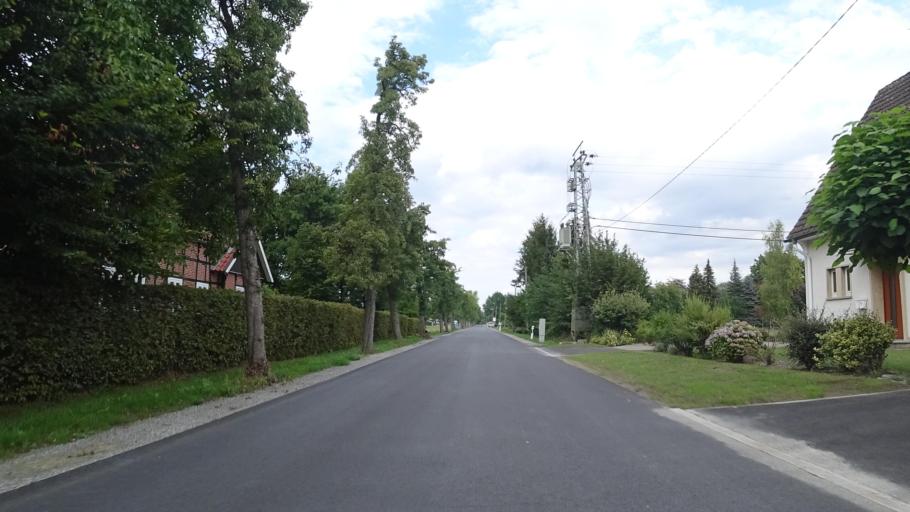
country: DE
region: North Rhine-Westphalia
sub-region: Regierungsbezirk Detmold
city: Steinhagen
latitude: 51.9589
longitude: 8.4273
